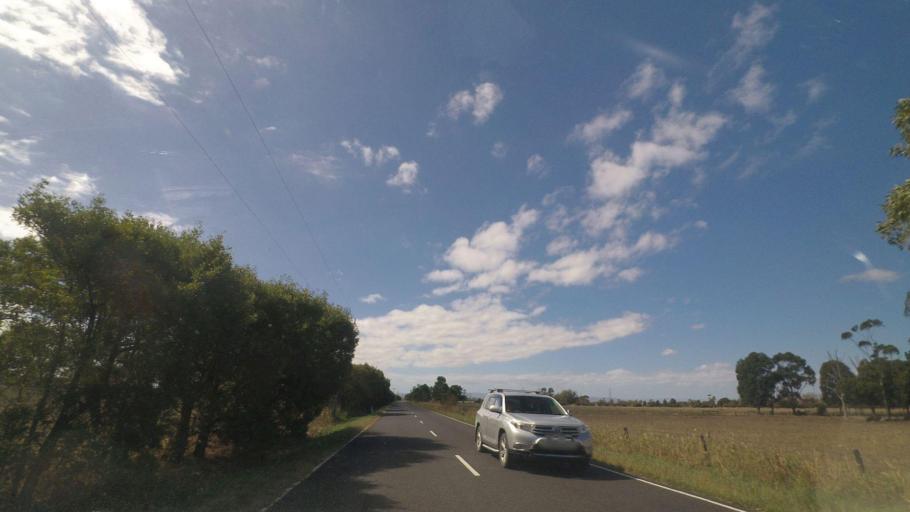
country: AU
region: Victoria
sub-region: Cardinia
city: Garfield
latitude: -38.2230
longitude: 145.6408
